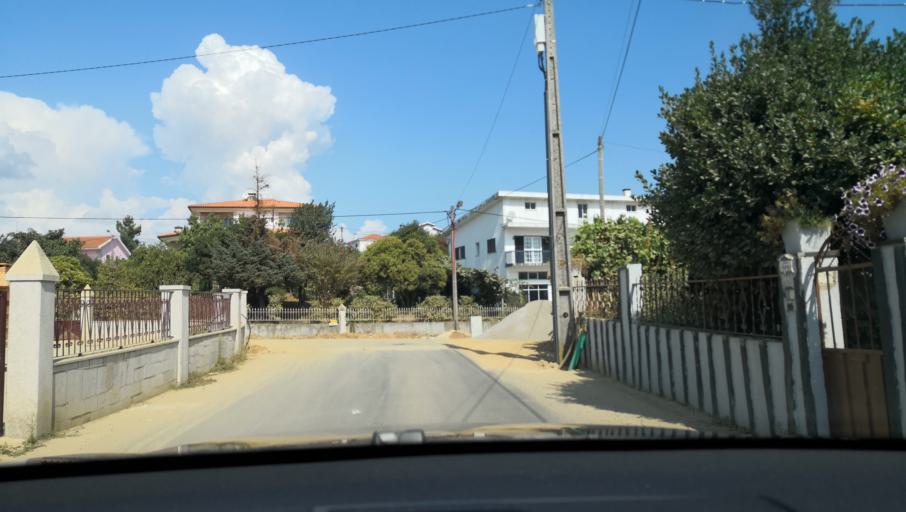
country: PT
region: Vila Real
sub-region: Sabrosa
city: Sabrosa
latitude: 41.2639
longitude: -7.6119
